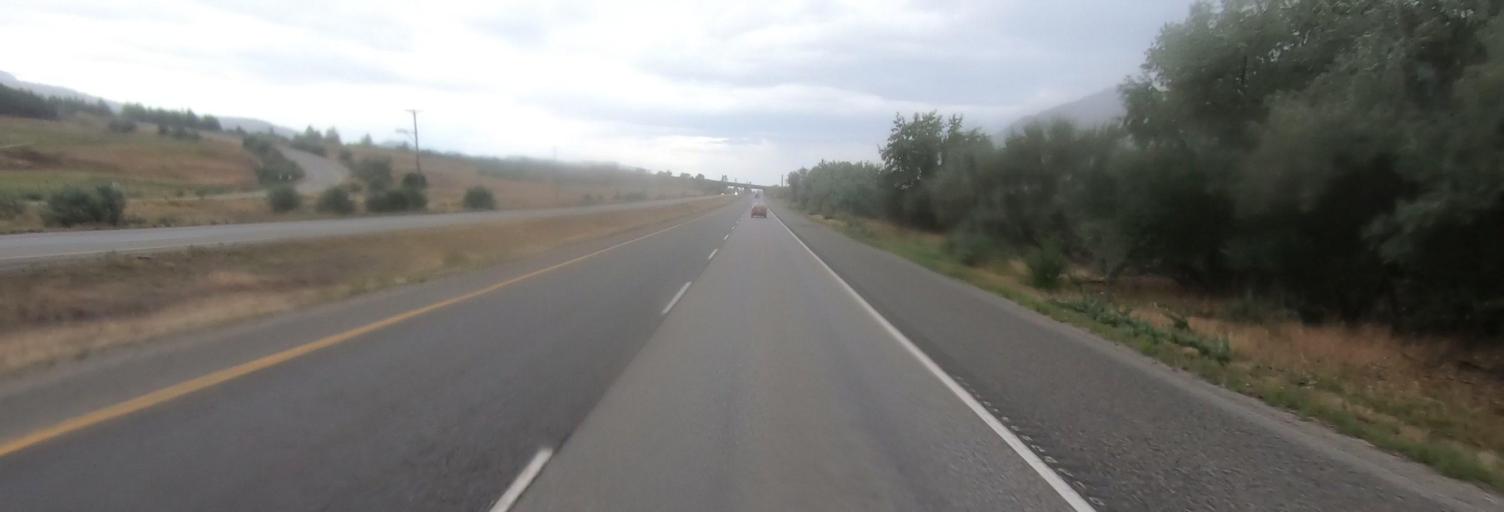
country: CA
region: British Columbia
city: Chase
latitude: 50.6476
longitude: -119.9377
